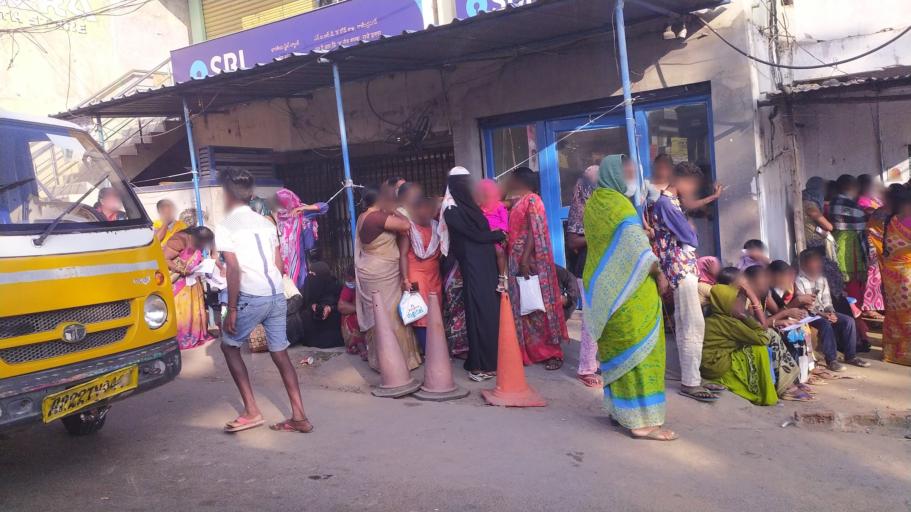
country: IN
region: Telangana
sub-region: Hyderabad
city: Hyderabad
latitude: 17.3221
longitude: 78.4024
